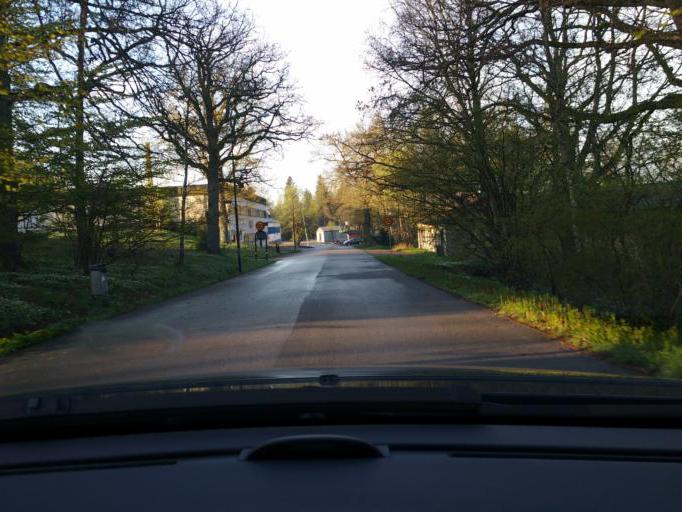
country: SE
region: Kronoberg
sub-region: Vaxjo Kommun
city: Lammhult
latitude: 57.1634
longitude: 14.5862
